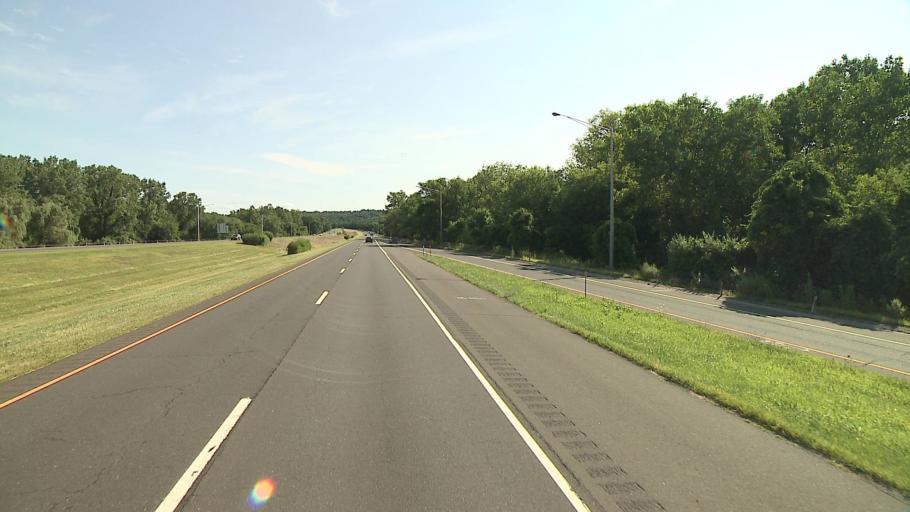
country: US
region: Connecticut
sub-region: Fairfield County
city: Danbury
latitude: 41.4324
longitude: -73.4084
